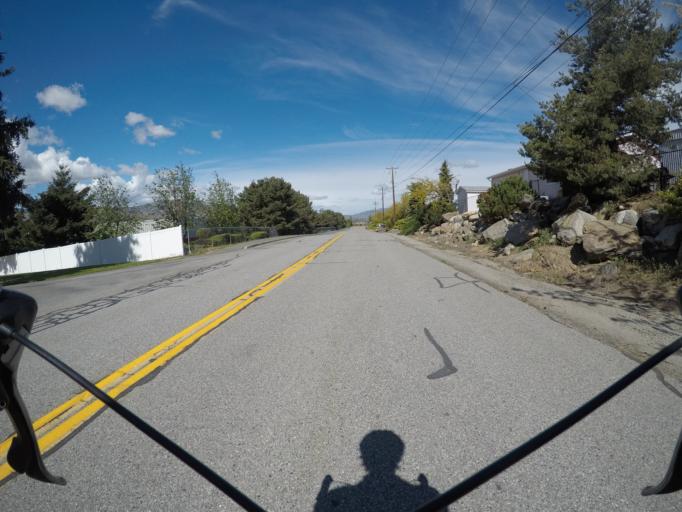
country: US
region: Washington
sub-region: Chelan County
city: South Wenatchee
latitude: 47.4015
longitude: -120.2781
